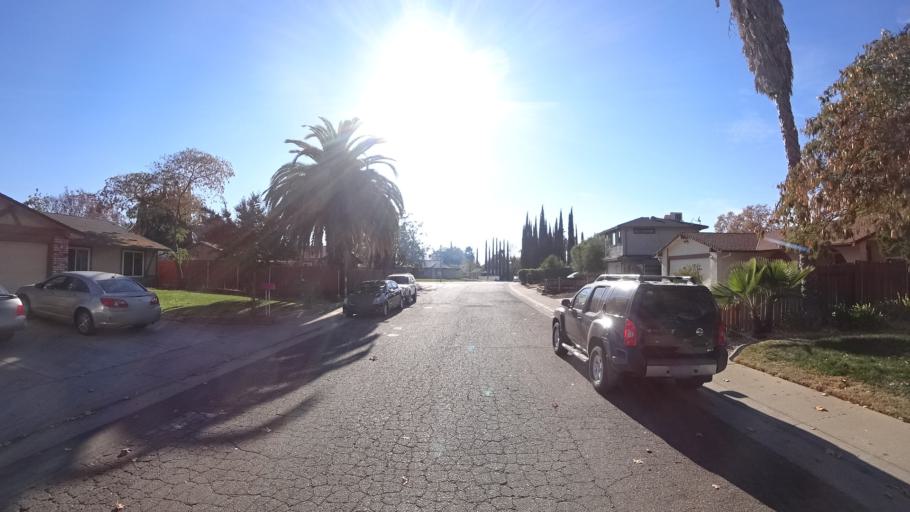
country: US
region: California
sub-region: Sacramento County
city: Antelope
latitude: 38.7031
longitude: -121.3176
